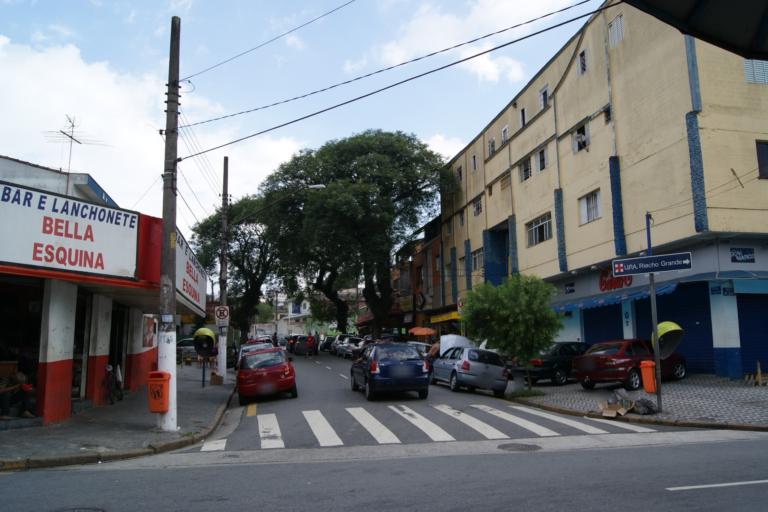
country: BR
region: Sao Paulo
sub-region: Sao Bernardo Do Campo
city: Sao Bernardo do Campo
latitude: -23.7792
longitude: -46.5308
